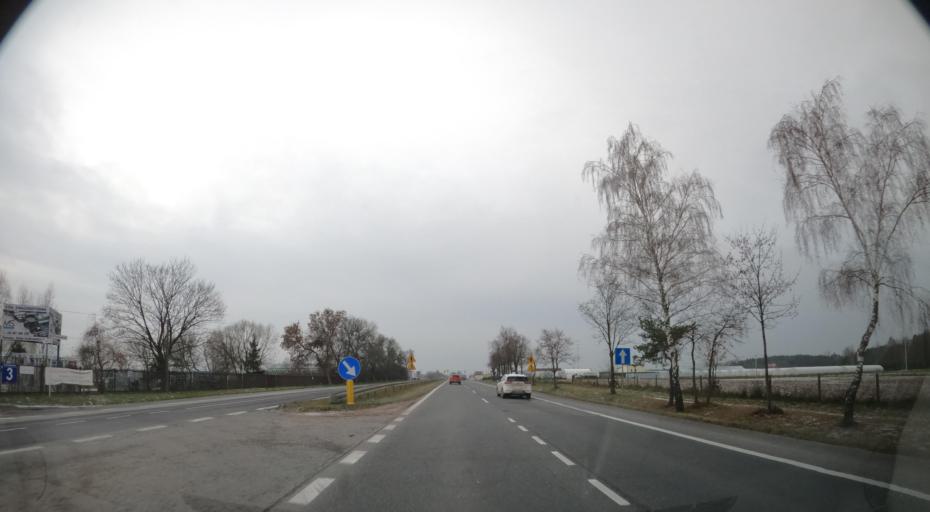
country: PL
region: Masovian Voivodeship
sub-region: Powiat piaseczynski
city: Tarczyn
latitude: 52.0002
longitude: 20.8432
